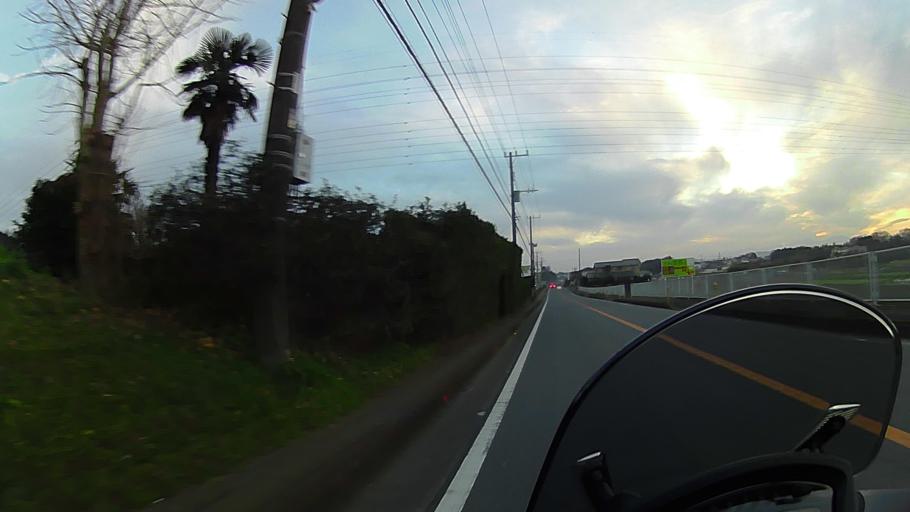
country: JP
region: Kanagawa
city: Atsugi
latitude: 35.4132
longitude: 139.4172
